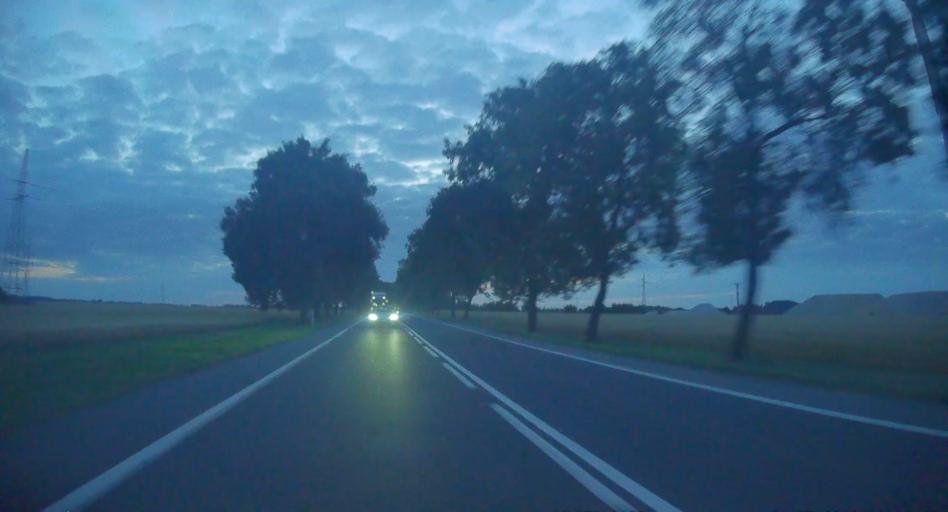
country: PL
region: Silesian Voivodeship
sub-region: Powiat klobucki
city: Klobuck
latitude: 50.9148
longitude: 18.8947
